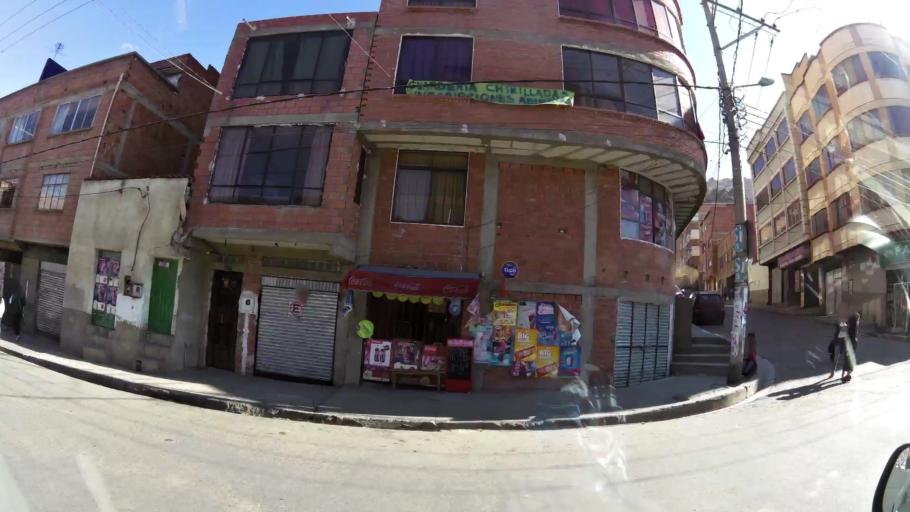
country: BO
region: La Paz
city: La Paz
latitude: -16.5142
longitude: -68.1410
